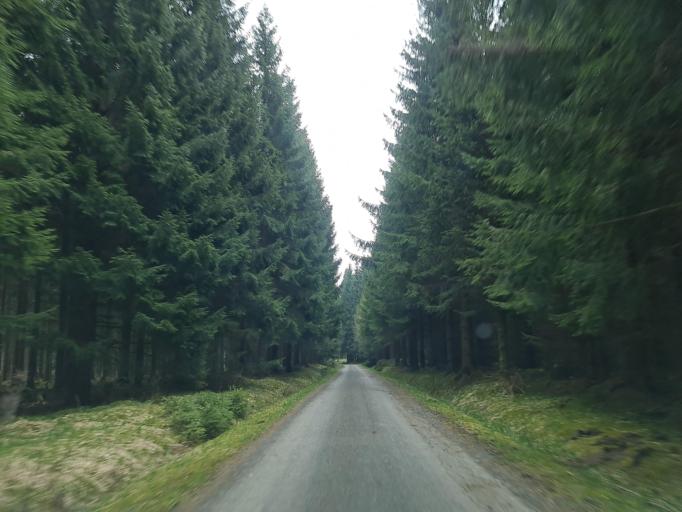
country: DE
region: Saxony
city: Grunbach
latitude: 50.4511
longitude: 12.3869
